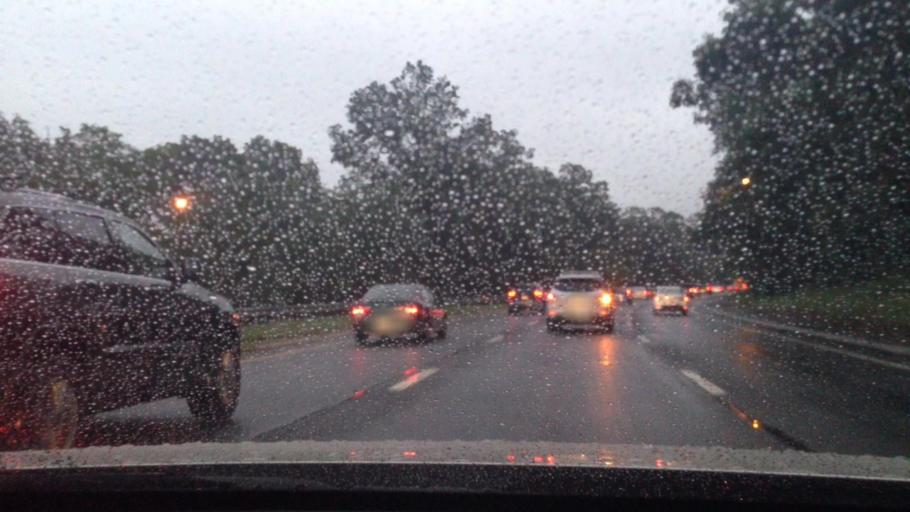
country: US
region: New York
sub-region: Nassau County
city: North Bellmore
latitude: 40.6997
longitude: -73.5296
